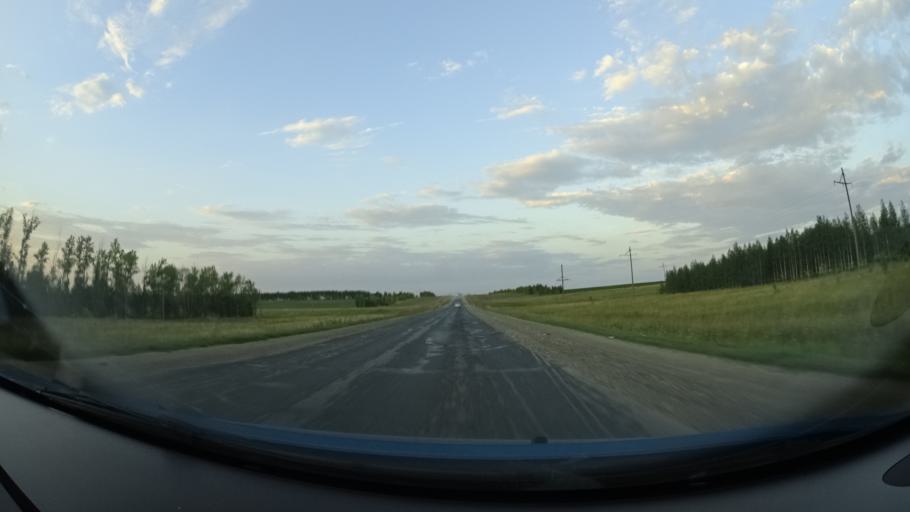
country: RU
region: Orenburg
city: Severnoye
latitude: 54.2222
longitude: 52.7398
